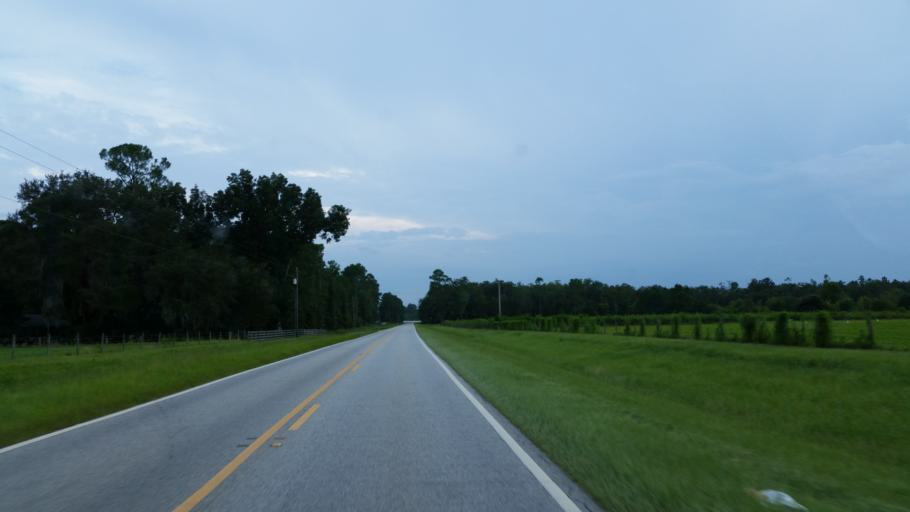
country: US
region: Georgia
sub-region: Lowndes County
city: Valdosta
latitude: 30.7651
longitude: -83.3036
